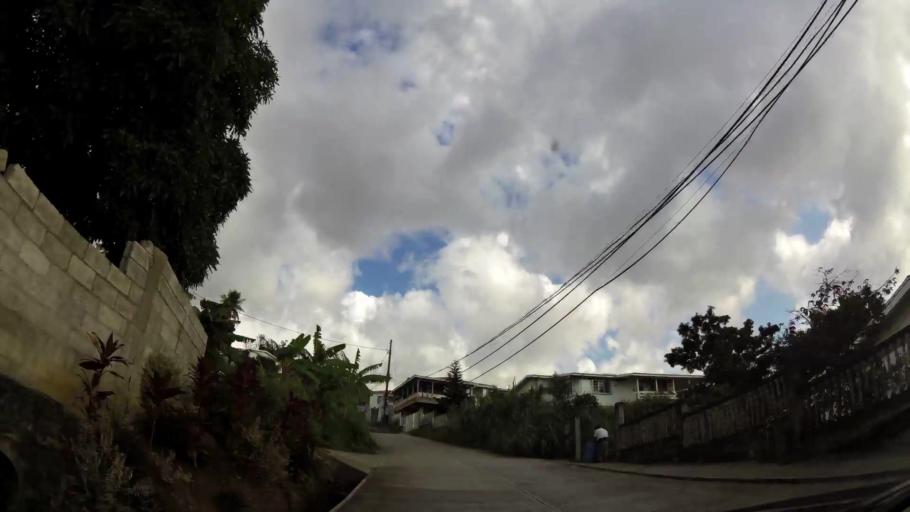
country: DM
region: Saint Paul
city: Mahaut
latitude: 15.3388
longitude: -61.3883
